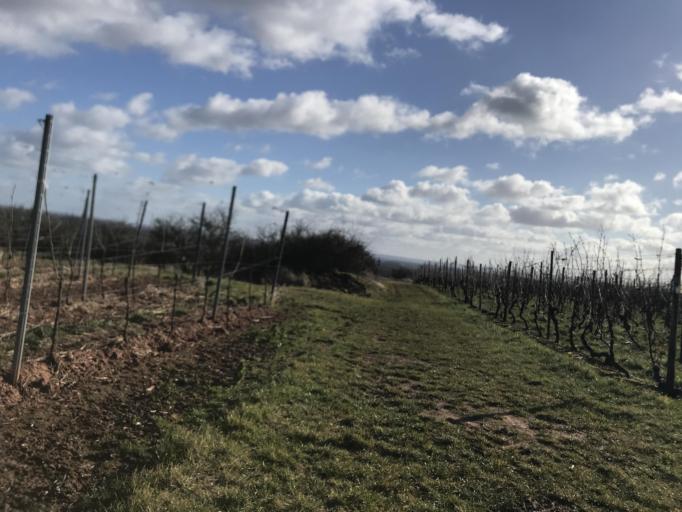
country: DE
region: Rheinland-Pfalz
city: Nackenheim
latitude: 49.9108
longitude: 8.3437
